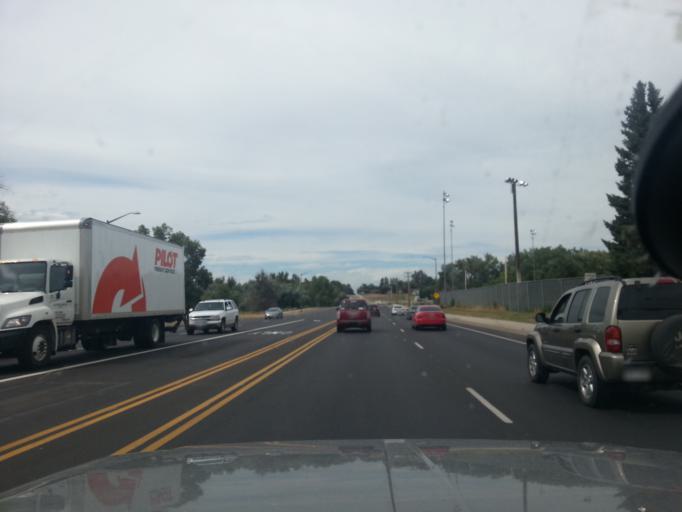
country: US
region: Colorado
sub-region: Larimer County
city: Loveland
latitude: 40.3929
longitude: -105.0968
